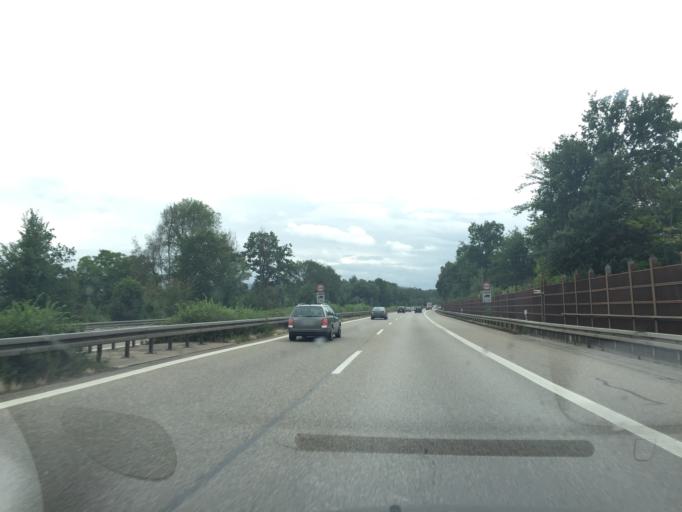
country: DE
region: Baden-Wuerttemberg
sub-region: Freiburg Region
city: Vorstetten
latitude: 48.0470
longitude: 7.8100
